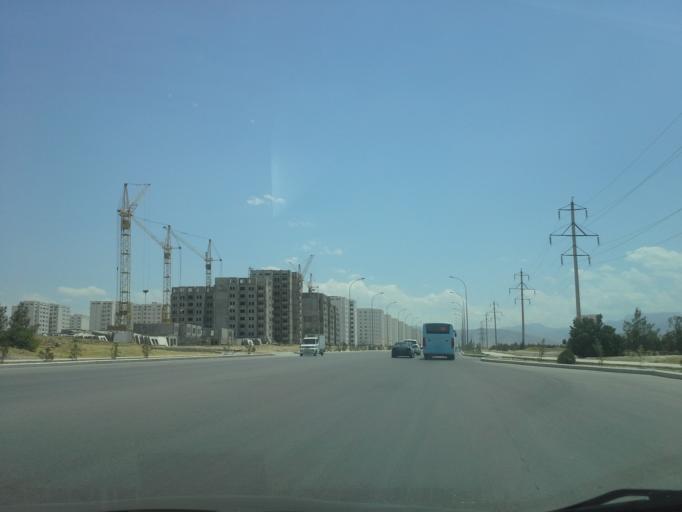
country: TM
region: Ahal
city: Ashgabat
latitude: 37.9000
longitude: 58.4056
